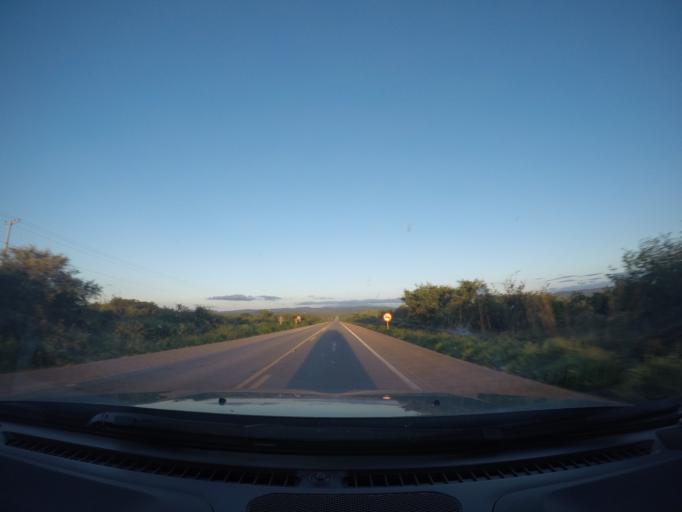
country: BR
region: Bahia
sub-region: Seabra
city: Seabra
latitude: -12.4030
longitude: -41.9503
